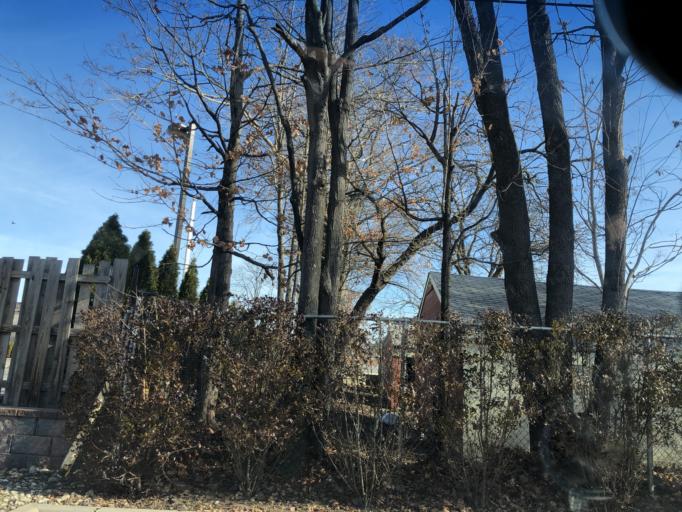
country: US
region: New Jersey
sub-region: Bergen County
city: Elmwood Park
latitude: 40.9171
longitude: -74.1281
